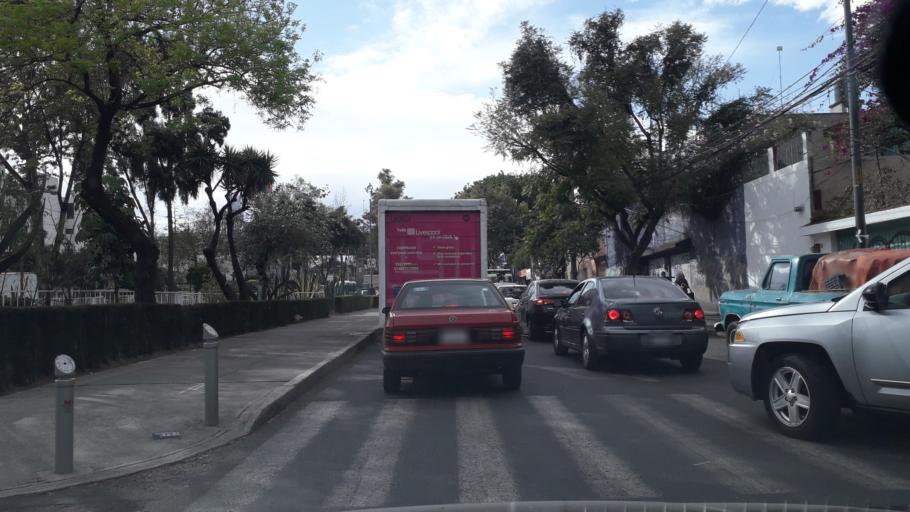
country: MX
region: Mexico City
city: Alvaro Obregon
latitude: 19.3761
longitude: -99.1898
